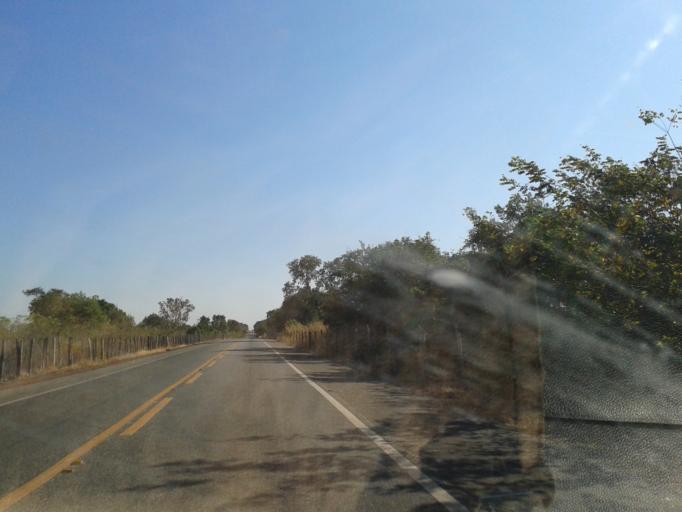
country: BR
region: Goias
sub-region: Mozarlandia
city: Mozarlandia
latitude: -14.7957
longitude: -50.5355
